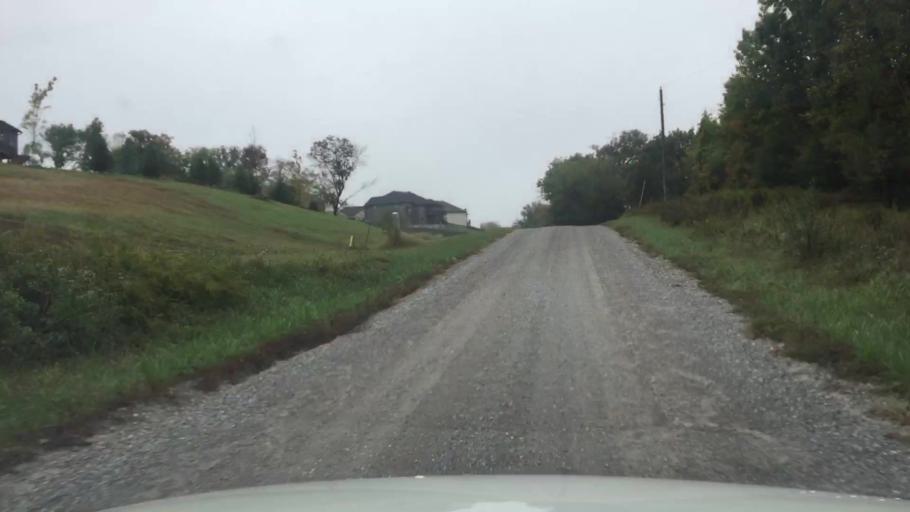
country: US
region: Missouri
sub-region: Boone County
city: Columbia
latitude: 38.8913
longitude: -92.4195
